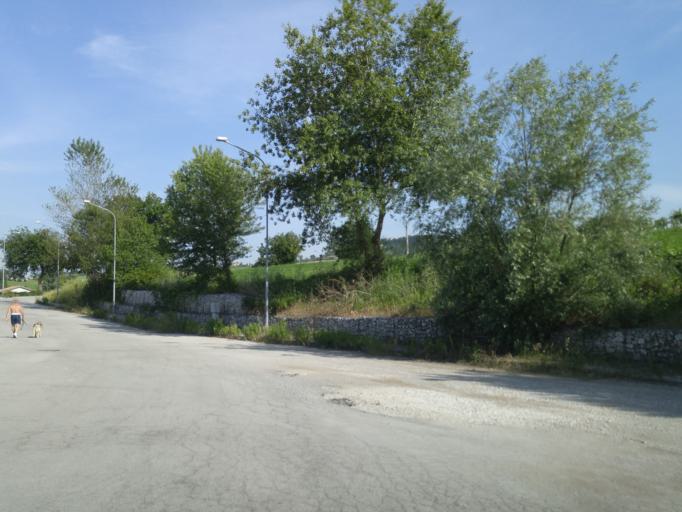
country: IT
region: The Marches
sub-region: Provincia di Pesaro e Urbino
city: Sant'Ippolito
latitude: 43.7030
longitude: 12.8807
